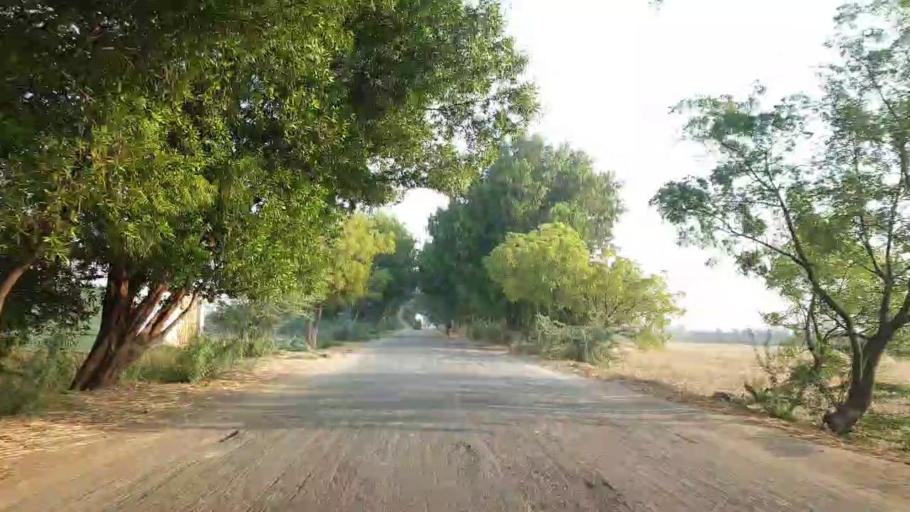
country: PK
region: Sindh
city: Tando Bago
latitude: 24.7723
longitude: 68.9592
